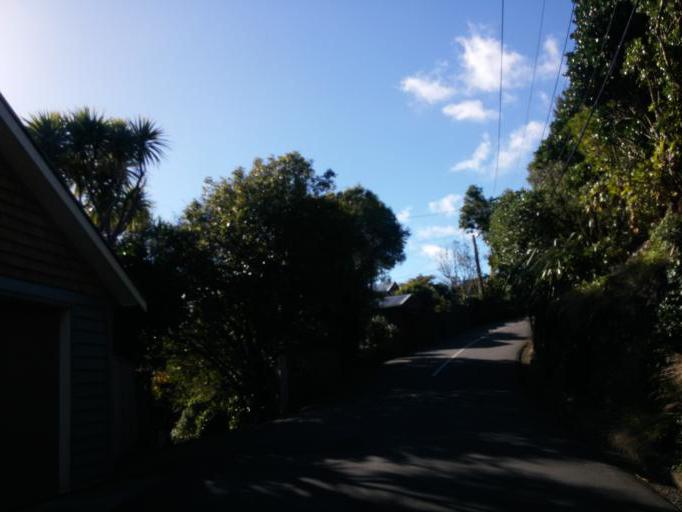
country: NZ
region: Wellington
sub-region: Wellington City
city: Kelburn
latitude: -41.2808
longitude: 174.7549
